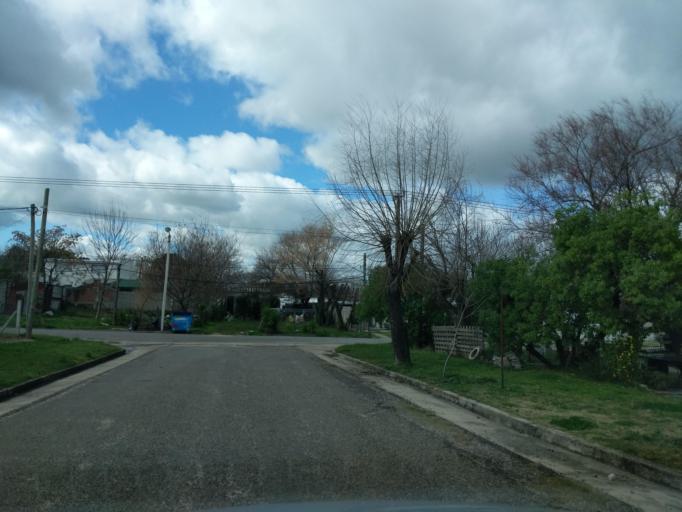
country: UY
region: Florida
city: Florida
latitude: -34.0915
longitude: -56.2311
